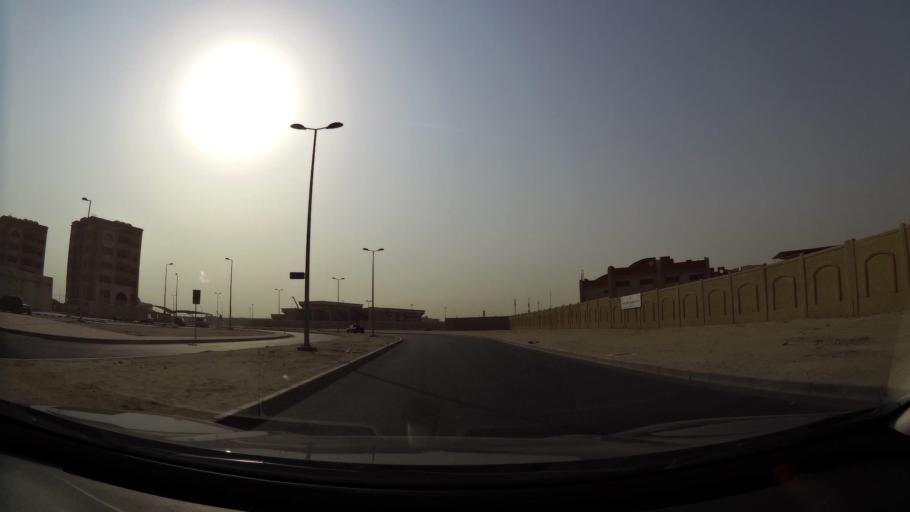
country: KW
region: Al Asimah
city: Ar Rabiyah
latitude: 29.3228
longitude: 47.8171
